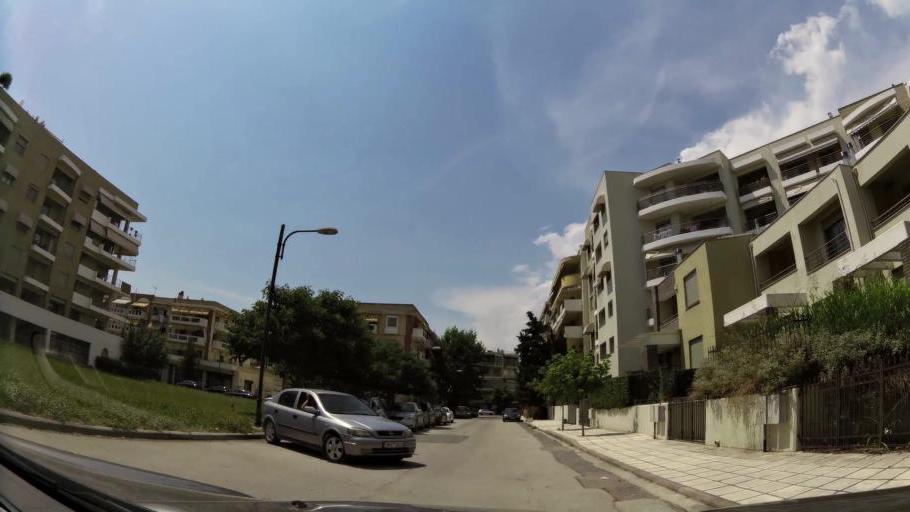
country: GR
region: Central Macedonia
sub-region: Nomos Thessalonikis
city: Ampelokipoi
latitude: 40.6602
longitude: 22.9245
